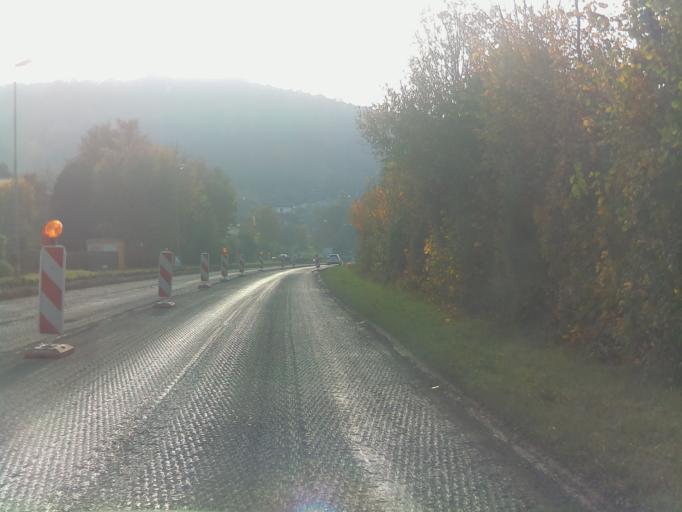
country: DE
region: Baden-Wuerttemberg
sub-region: Karlsruhe Region
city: Mosbach
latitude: 49.3820
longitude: 9.1878
